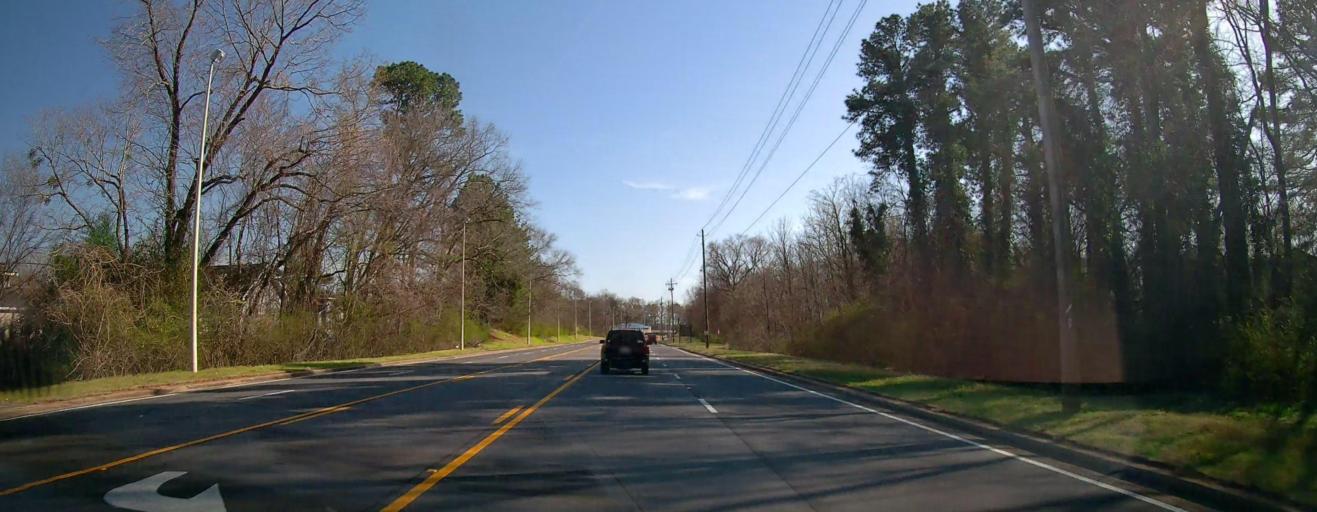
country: US
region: Alabama
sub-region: Lauderdale County
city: East Florence
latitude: 34.8180
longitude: -87.6266
